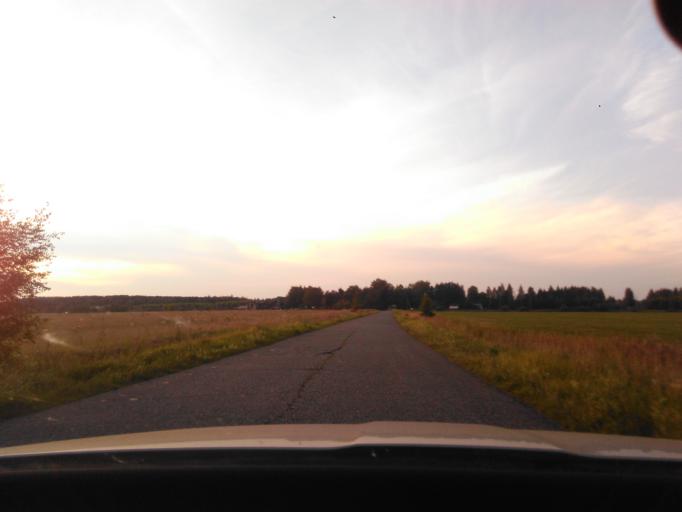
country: RU
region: Tverskaya
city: Zavidovo
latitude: 56.6050
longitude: 36.5939
